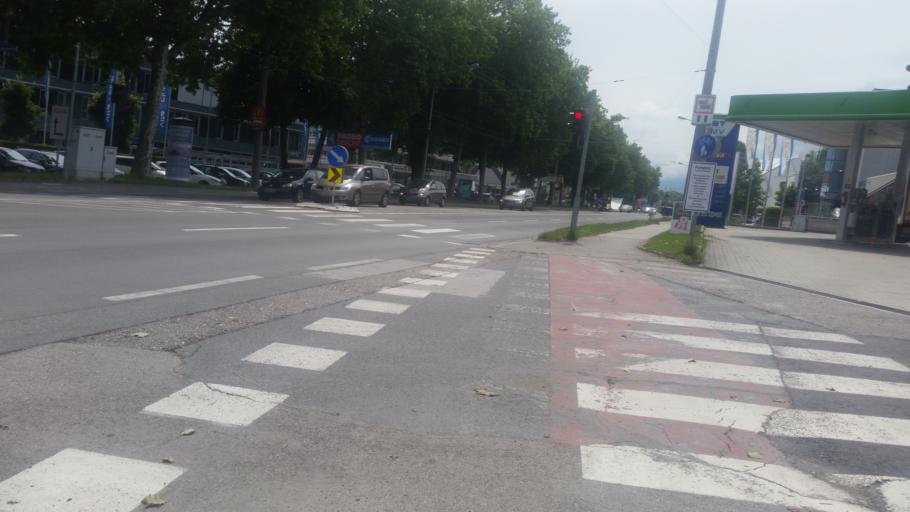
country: AT
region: Salzburg
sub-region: Politischer Bezirk Salzburg-Umgebung
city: Anif
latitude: 47.7765
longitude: 13.0684
